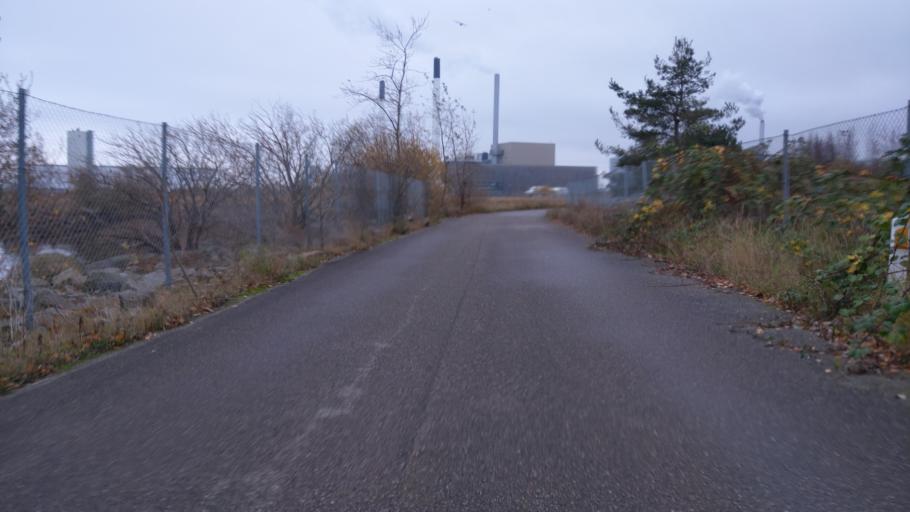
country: DK
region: Capital Region
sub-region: Kobenhavn
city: Christianshavn
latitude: 55.6949
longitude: 12.6249
